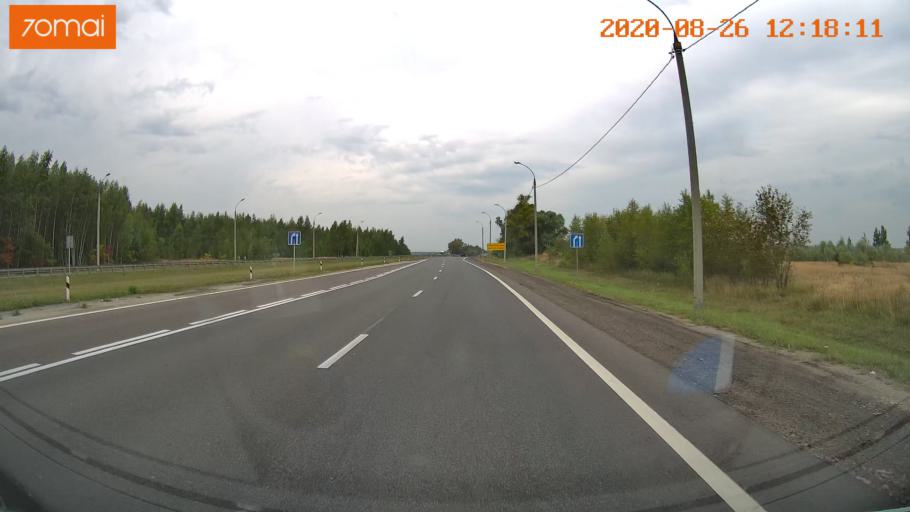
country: RU
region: Rjazan
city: Murmino
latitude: 54.4705
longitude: 40.0224
